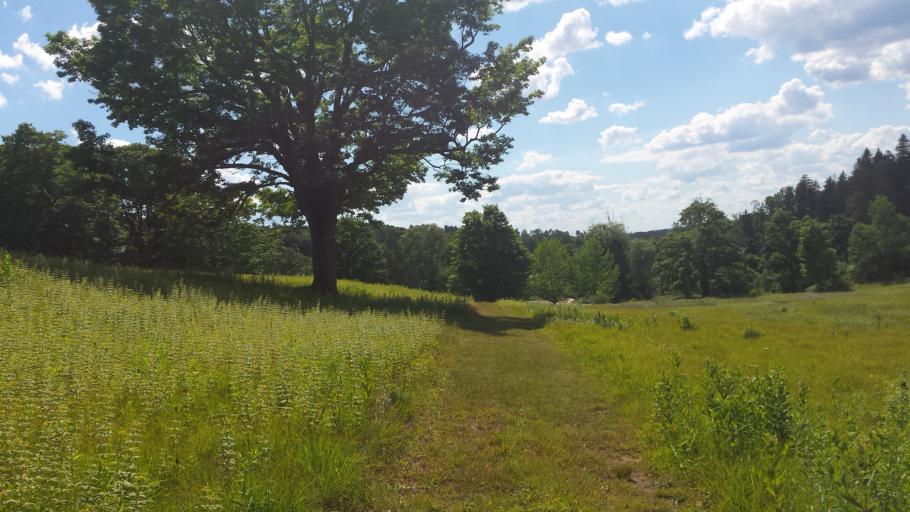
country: US
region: New York
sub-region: Westchester County
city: Pound Ridge
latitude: 41.2584
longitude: -73.5862
